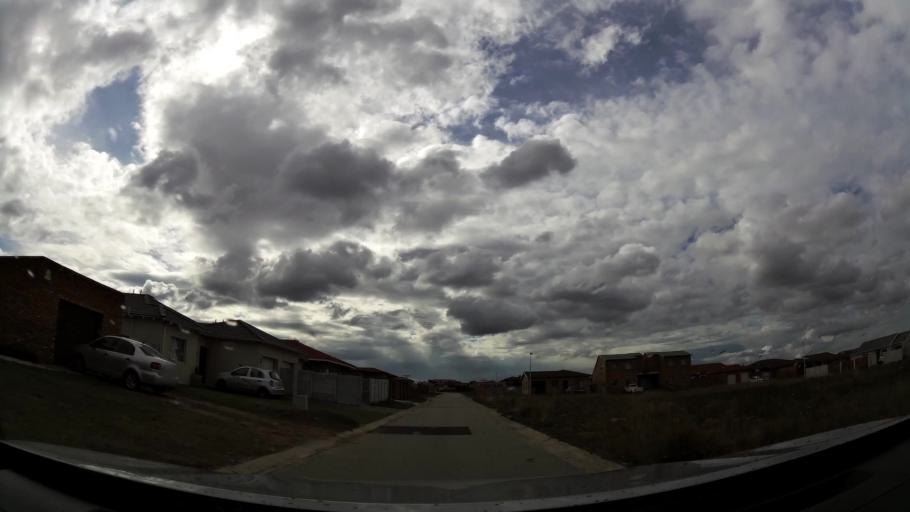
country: ZA
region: Eastern Cape
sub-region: Nelson Mandela Bay Metropolitan Municipality
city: Port Elizabeth
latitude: -33.9296
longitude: 25.5071
